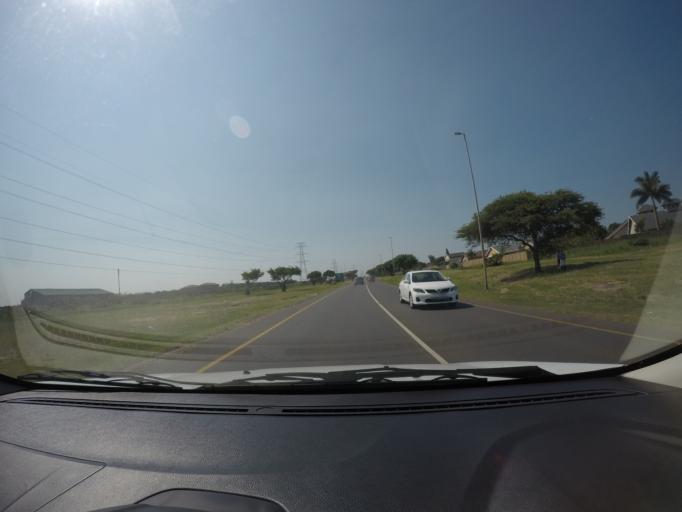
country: ZA
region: KwaZulu-Natal
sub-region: uThungulu District Municipality
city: Richards Bay
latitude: -28.7346
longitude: 32.0403
